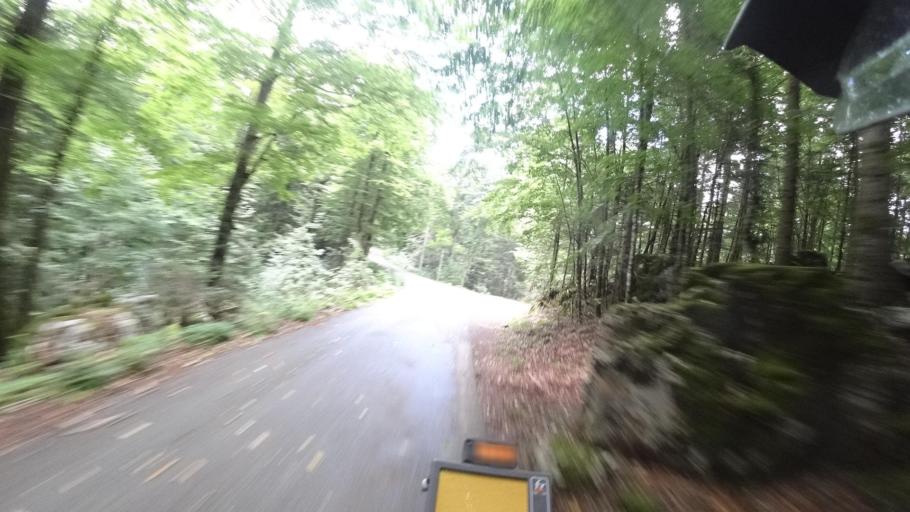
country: HR
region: Licko-Senjska
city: Senj
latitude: 45.0986
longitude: 14.9629
